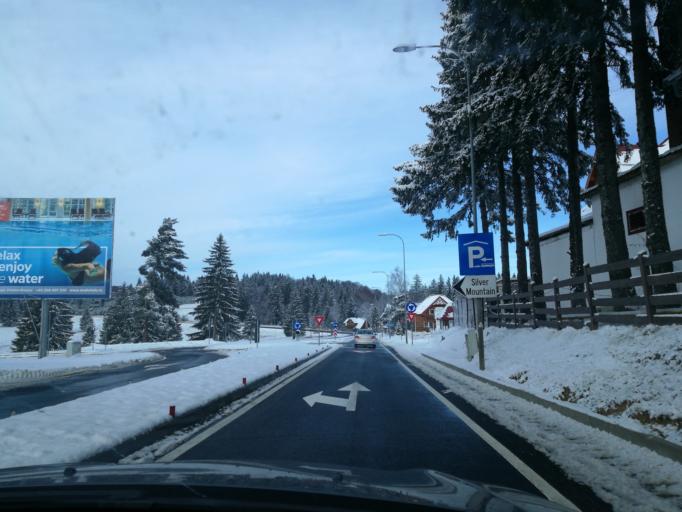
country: RO
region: Brasov
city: Brasov
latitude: 45.6088
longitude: 25.5537
